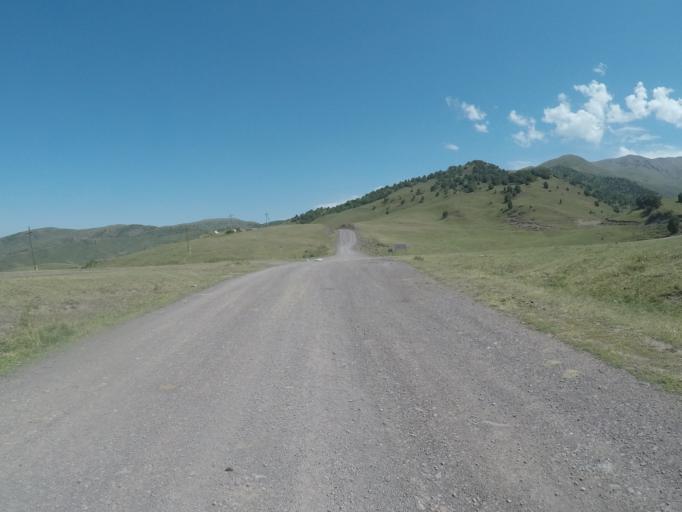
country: KG
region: Chuy
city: Bishkek
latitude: 42.6502
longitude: 74.5303
